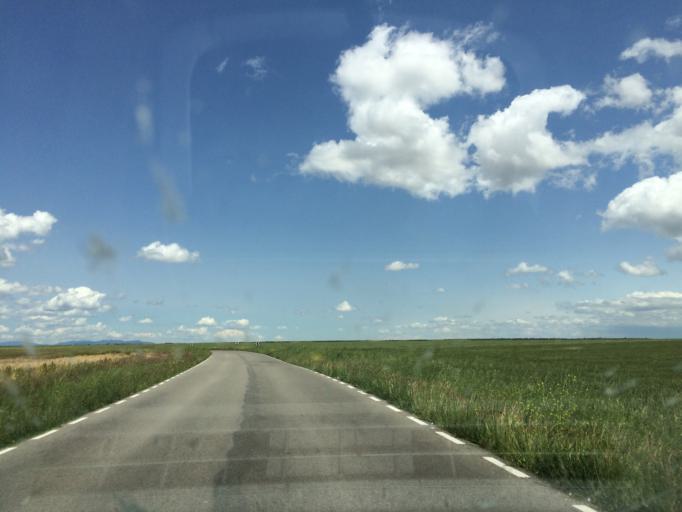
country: ES
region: Madrid
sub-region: Provincia de Madrid
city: Valdepielagos
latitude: 40.7186
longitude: -3.4196
